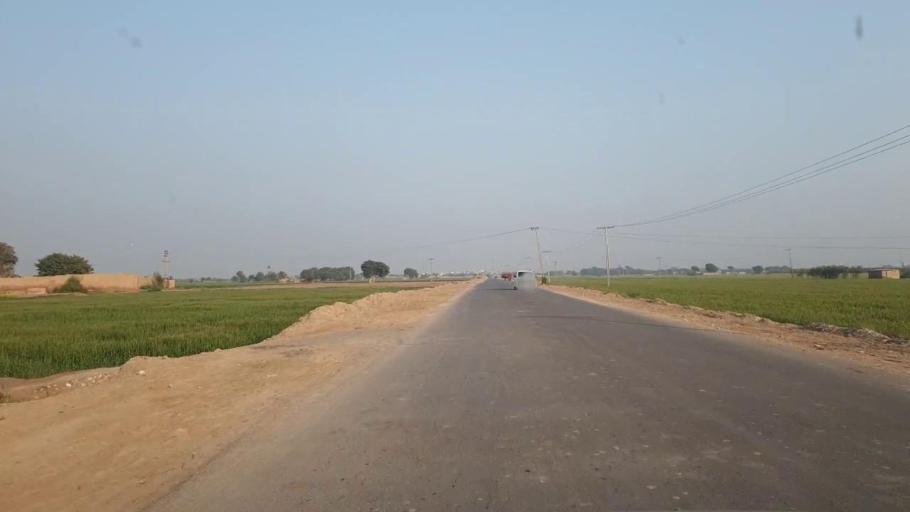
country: PK
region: Sindh
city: Bhit Shah
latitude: 25.8082
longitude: 68.4705
